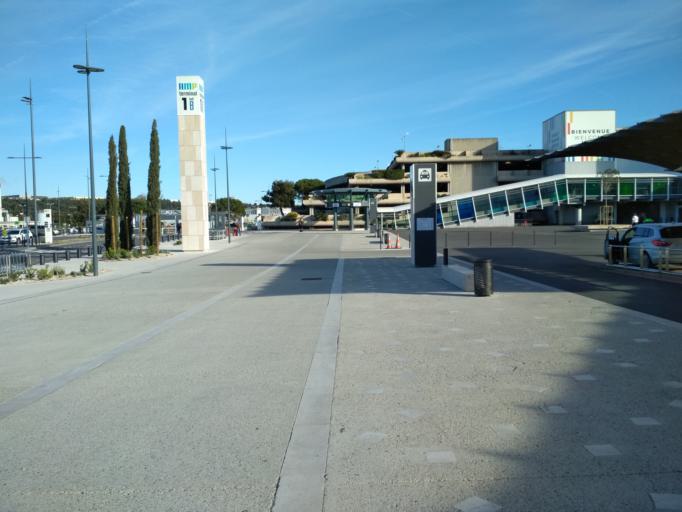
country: FR
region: Provence-Alpes-Cote d'Azur
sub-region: Departement des Bouches-du-Rhone
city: Saint-Victoret
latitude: 43.4411
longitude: 5.2229
